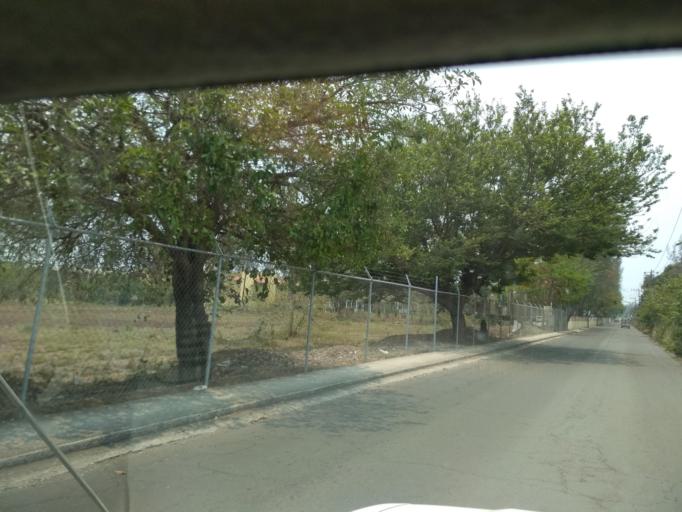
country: MX
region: Veracruz
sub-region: Veracruz
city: Las Amapolas
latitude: 19.1583
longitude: -96.2088
